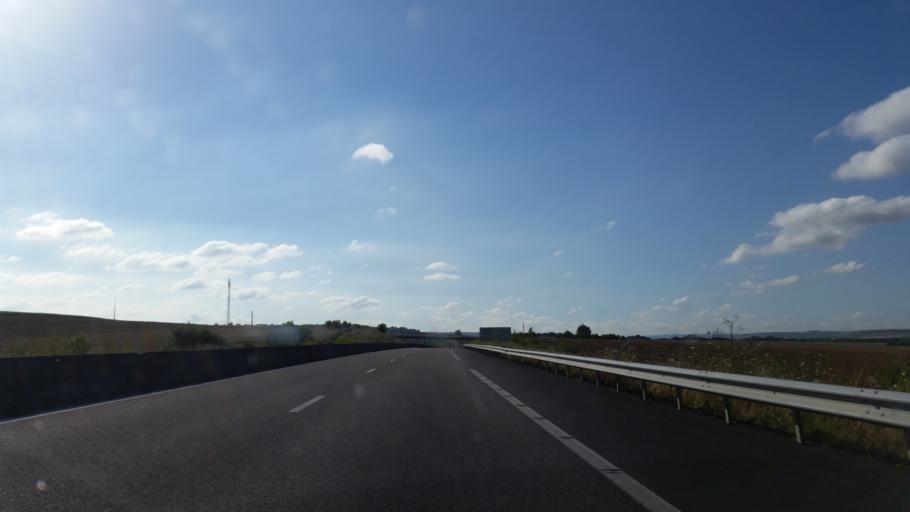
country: FR
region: Haute-Normandie
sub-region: Departement de la Seine-Maritime
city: Serqueux
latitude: 49.7367
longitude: 1.5487
